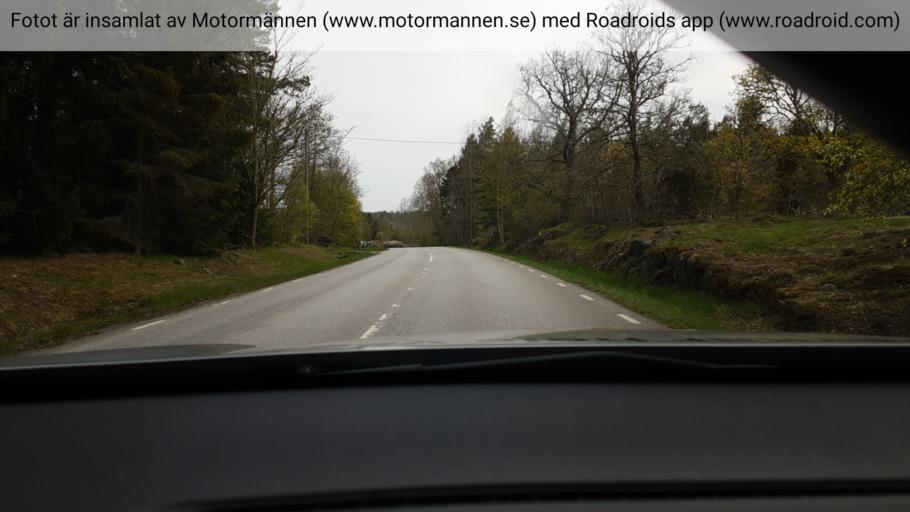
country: SE
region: Stockholm
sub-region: Vallentuna Kommun
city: Vallentuna
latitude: 59.7676
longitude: 18.0412
